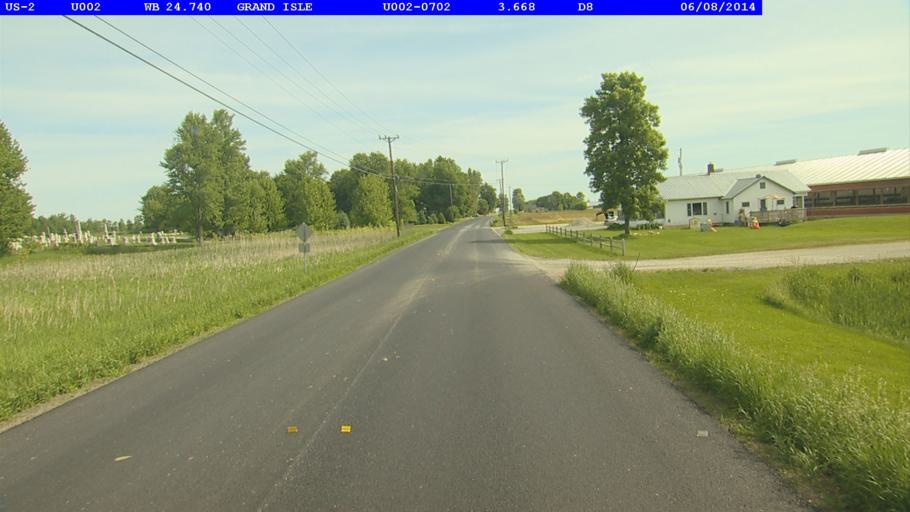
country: US
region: Vermont
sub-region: Grand Isle County
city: North Hero
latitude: 44.7153
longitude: -73.2972
